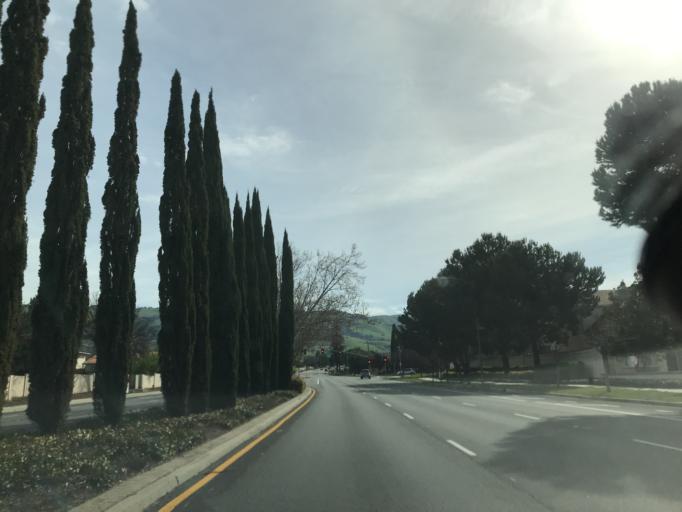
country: US
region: California
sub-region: Santa Clara County
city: Seven Trees
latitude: 37.3155
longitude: -121.7813
